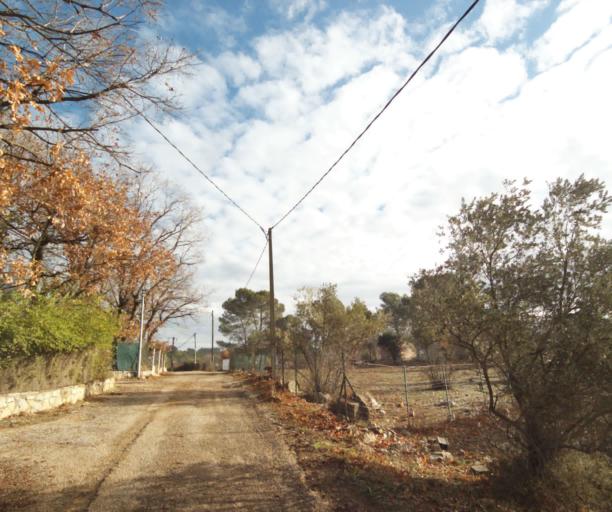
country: FR
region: Provence-Alpes-Cote d'Azur
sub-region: Departement du Var
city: Trans-en-Provence
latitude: 43.4926
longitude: 6.4725
